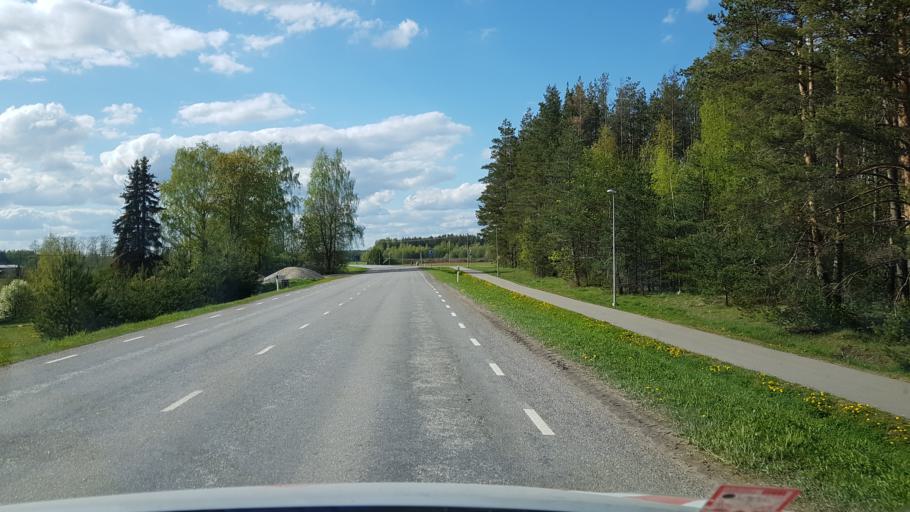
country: EE
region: Tartu
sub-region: UElenurme vald
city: Ulenurme
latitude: 58.3018
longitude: 26.8643
